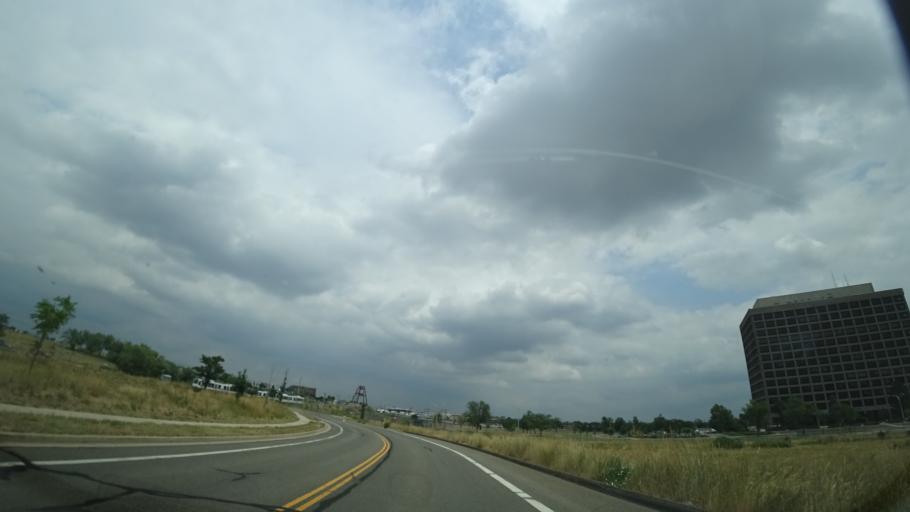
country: US
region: Colorado
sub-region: Jefferson County
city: Lakewood
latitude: 39.7218
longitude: -105.1264
